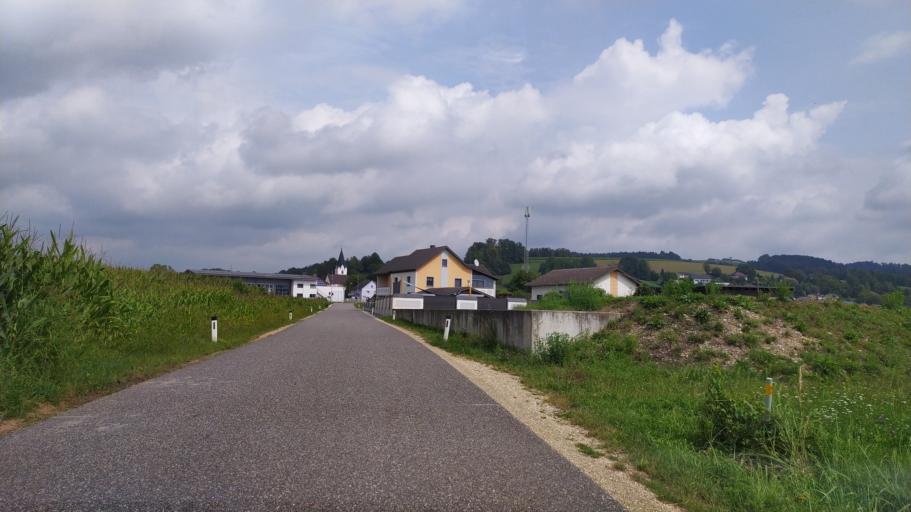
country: AT
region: Upper Austria
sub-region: Politischer Bezirk Perg
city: Bad Kreuzen
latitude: 48.2042
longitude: 14.7870
